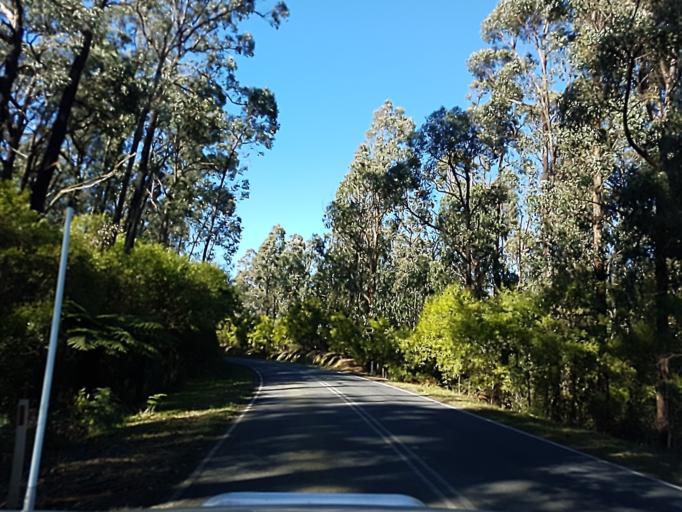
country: AU
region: Victoria
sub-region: Yarra Ranges
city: Yarra Glen
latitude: -37.5409
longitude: 145.3924
